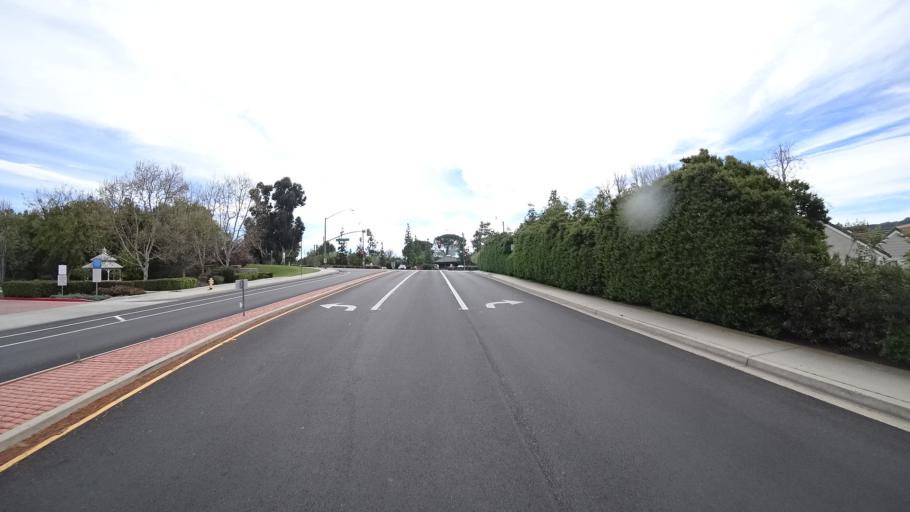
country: US
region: California
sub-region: Los Angeles County
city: Westlake Village
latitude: 34.1505
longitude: -118.8195
